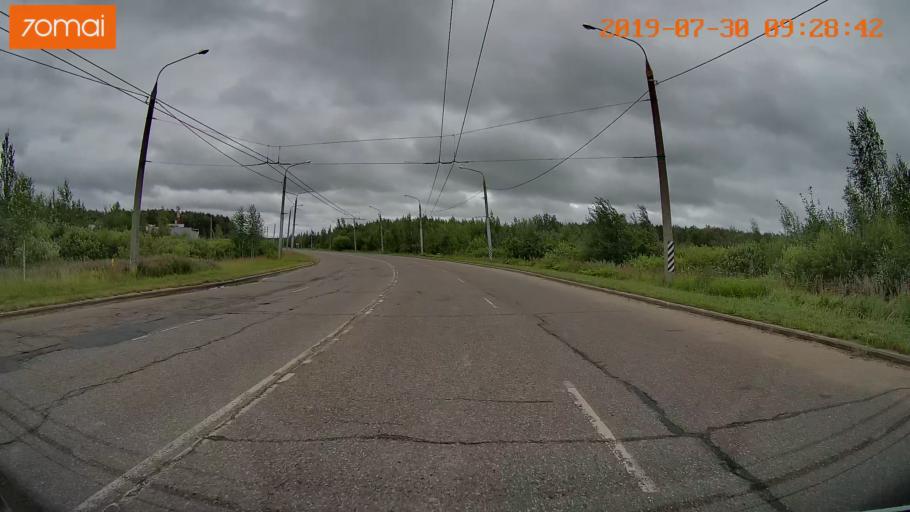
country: RU
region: Ivanovo
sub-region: Gorod Ivanovo
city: Ivanovo
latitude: 56.9519
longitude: 40.9480
